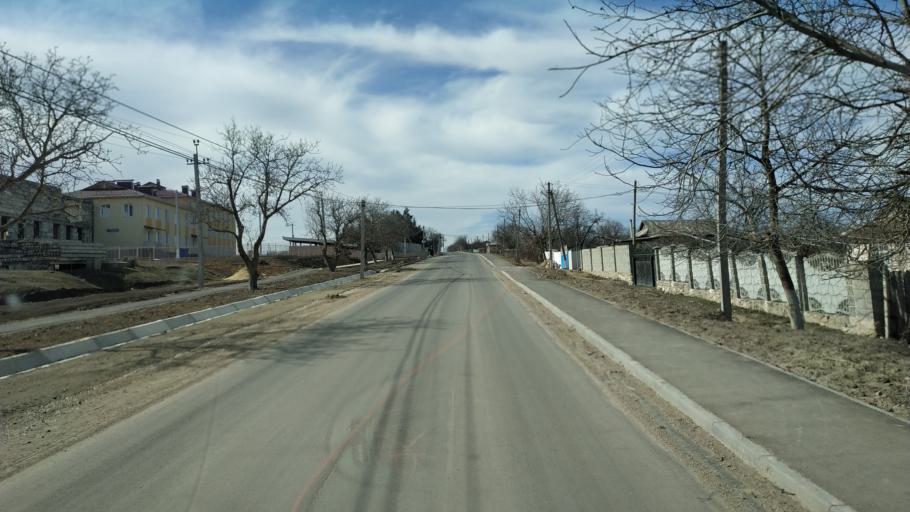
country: RO
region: Iasi
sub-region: Comuna Grozesti
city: Grozesti
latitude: 46.9641
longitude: 28.1634
